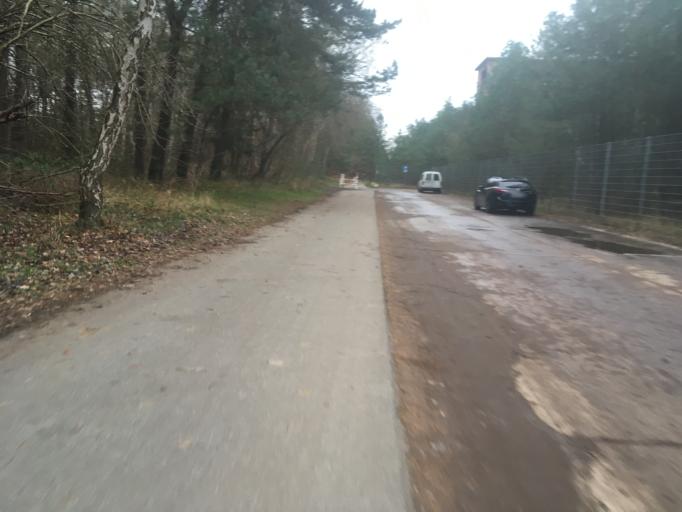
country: DE
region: Mecklenburg-Vorpommern
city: Sagard
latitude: 54.4573
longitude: 13.5673
